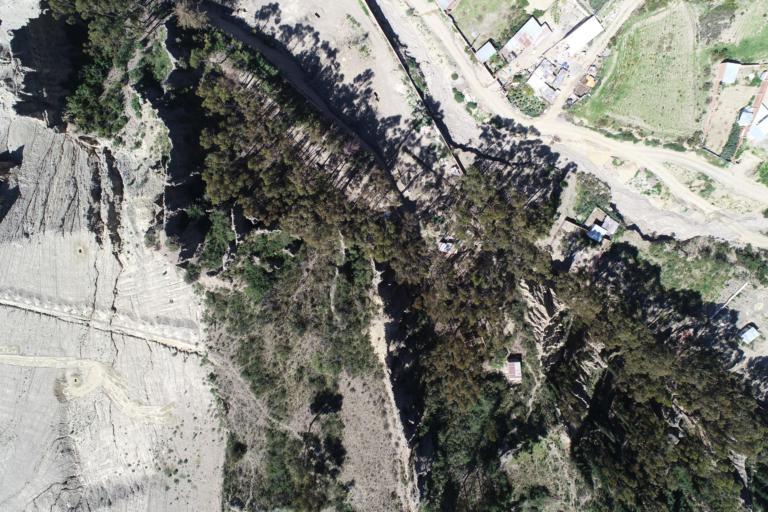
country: BO
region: La Paz
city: La Paz
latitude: -16.5077
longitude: -68.0584
